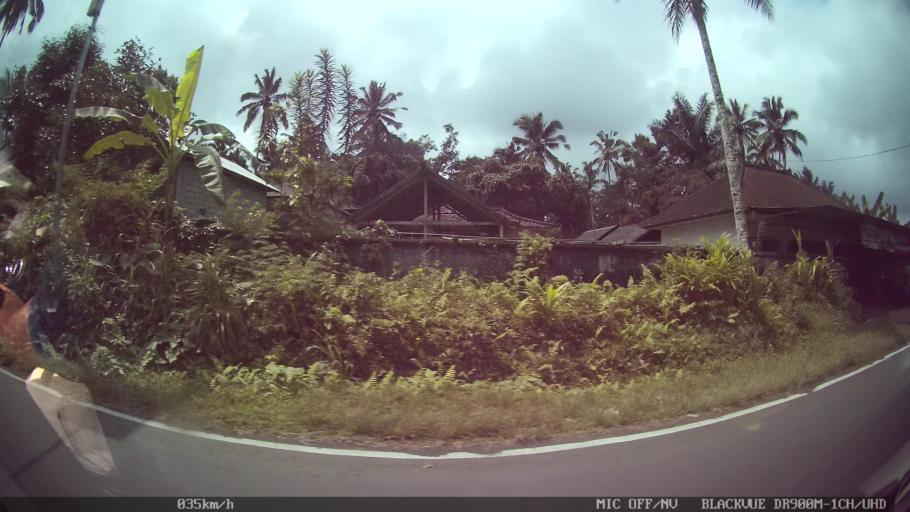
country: ID
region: Bali
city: Banjar Geriana Kangin
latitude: -8.4171
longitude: 115.4369
